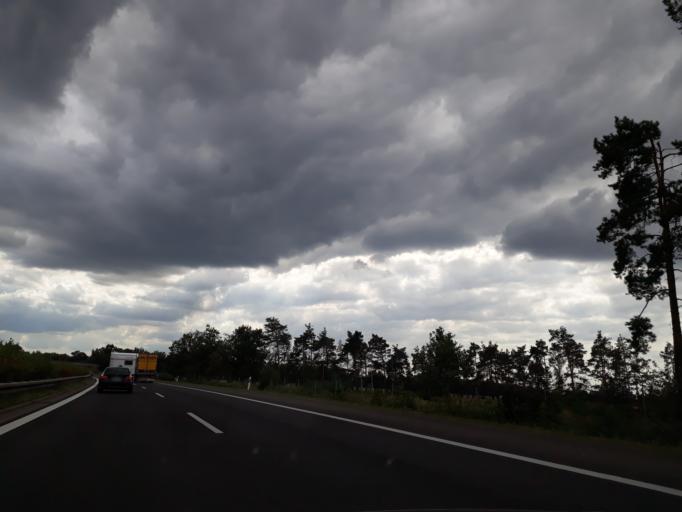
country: DE
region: Brandenburg
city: Bronkow
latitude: 51.6357
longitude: 13.9412
